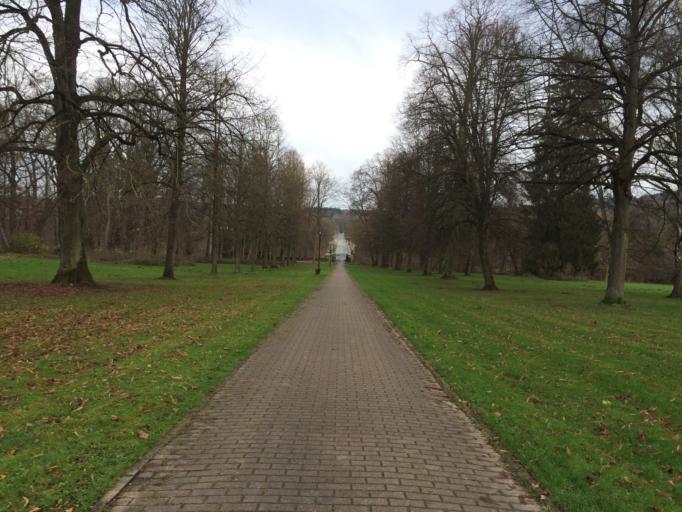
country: DE
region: North Rhine-Westphalia
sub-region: Regierungsbezirk Detmold
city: Schieder-Schwalenberg
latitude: 51.9183
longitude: 9.1502
